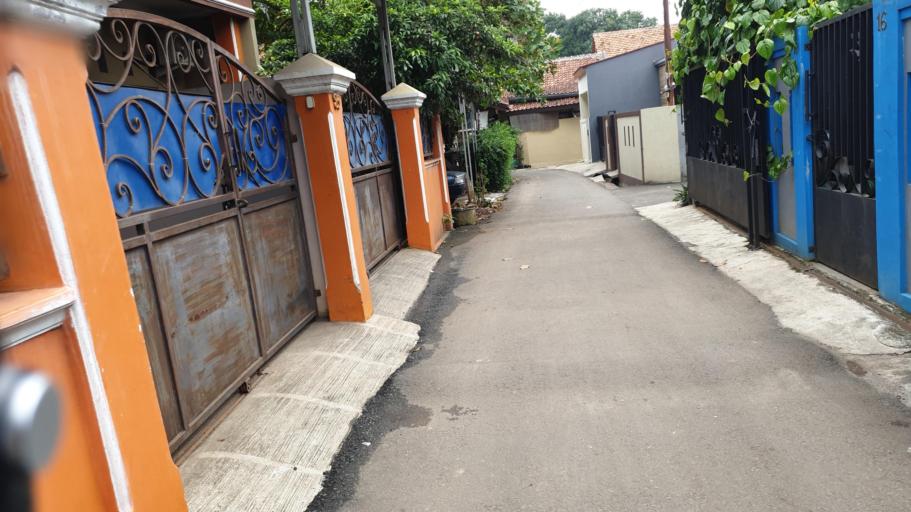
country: ID
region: West Java
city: Depok
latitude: -6.3241
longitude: 106.8263
